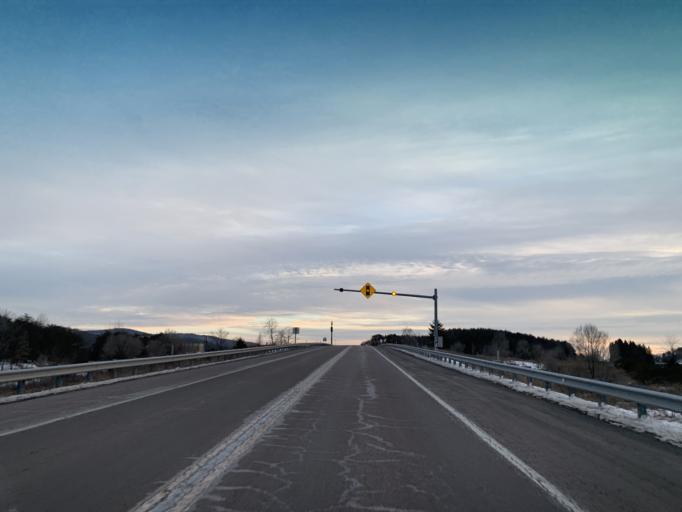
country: US
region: Maryland
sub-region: Allegany County
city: Cumberland
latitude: 39.6767
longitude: -78.7164
